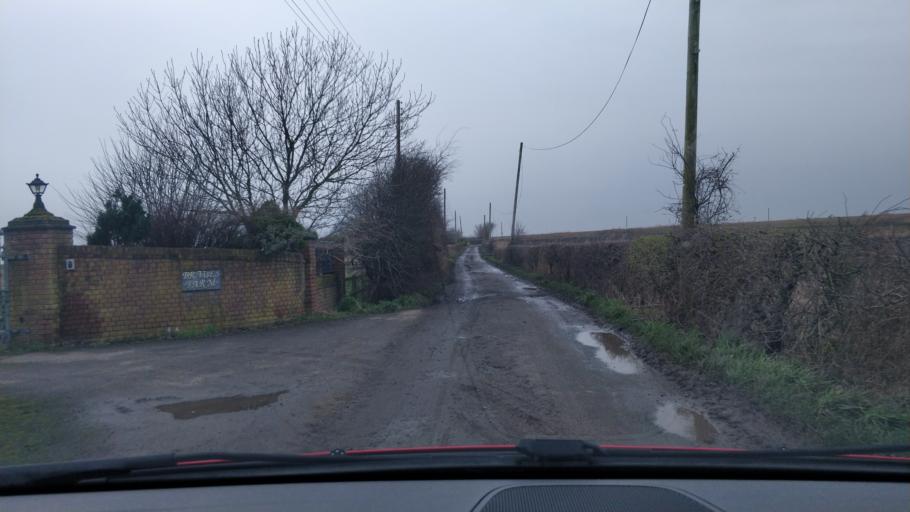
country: GB
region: England
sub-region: Lancashire
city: Banks
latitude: 53.6854
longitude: -2.9308
